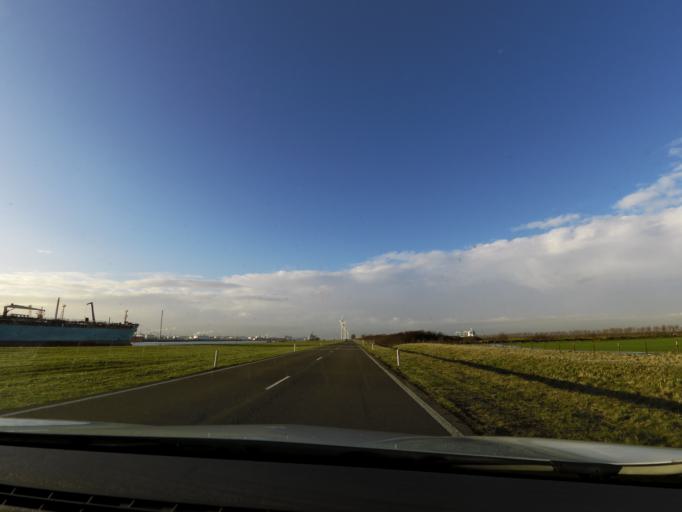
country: NL
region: South Holland
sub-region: Gemeente Westland
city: Maasdijk
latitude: 51.9350
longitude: 4.1953
